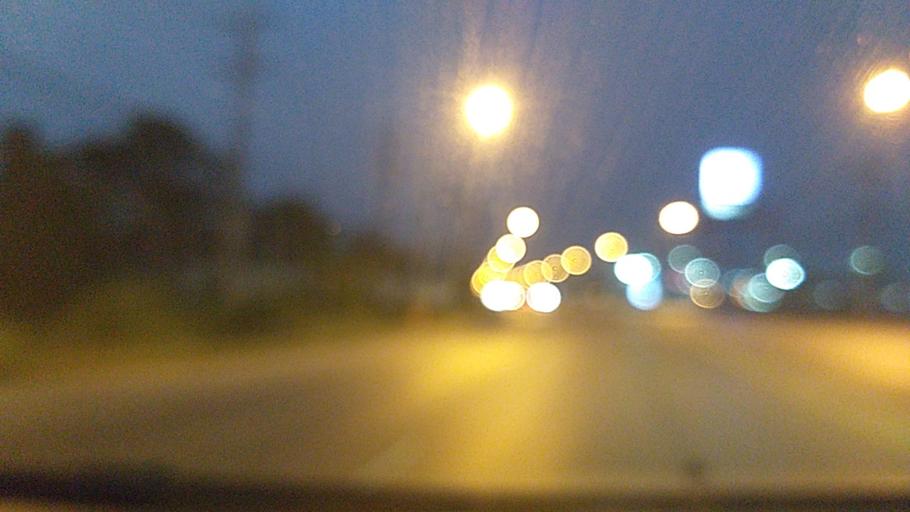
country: TH
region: Sing Buri
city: Sing Buri
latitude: 14.8606
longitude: 100.3942
